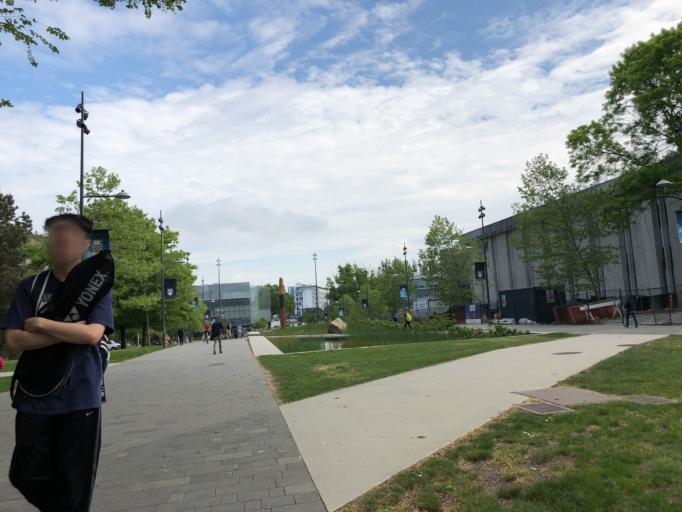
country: CA
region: British Columbia
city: West End
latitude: 49.2650
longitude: -123.2524
